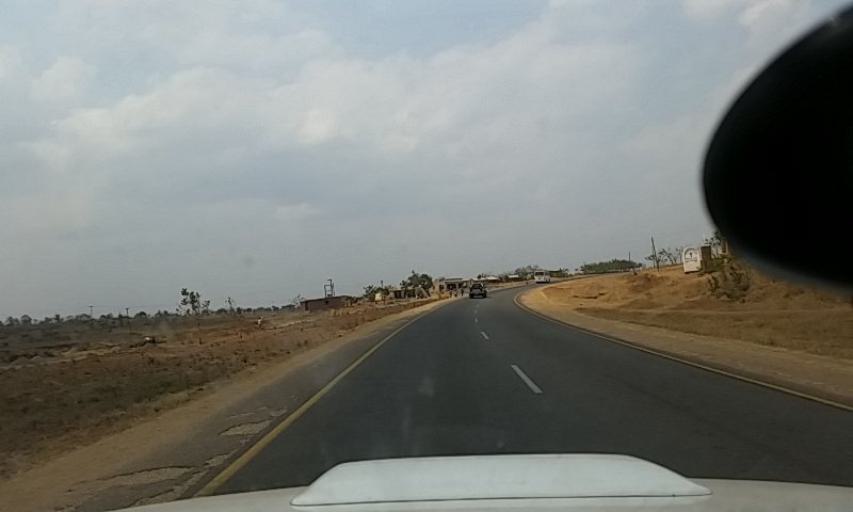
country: MW
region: Central Region
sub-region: Lilongwe District
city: Lilongwe
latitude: -13.8526
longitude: 33.8331
